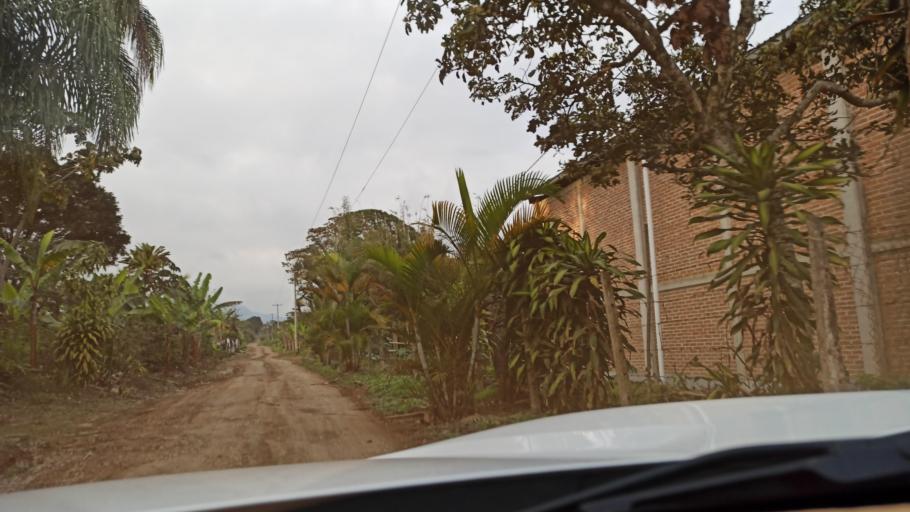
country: MX
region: Veracruz
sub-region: Fortin
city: Fortin de las Flores
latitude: 18.9195
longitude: -97.0038
